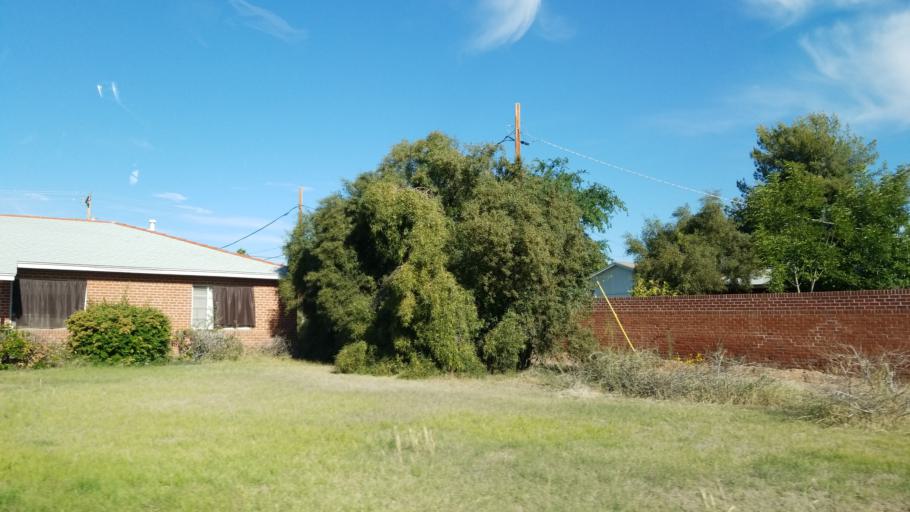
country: US
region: Arizona
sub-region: Maricopa County
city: Phoenix
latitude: 33.5189
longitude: -112.0856
